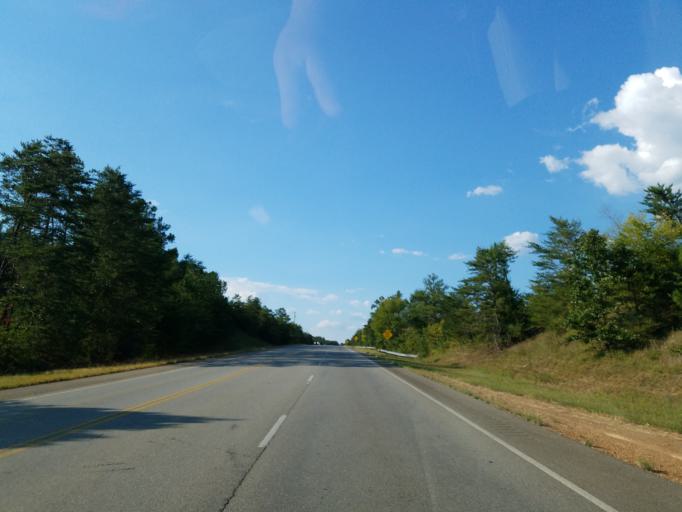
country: US
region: Georgia
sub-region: Murray County
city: Chatsworth
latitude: 34.6721
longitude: -84.7237
